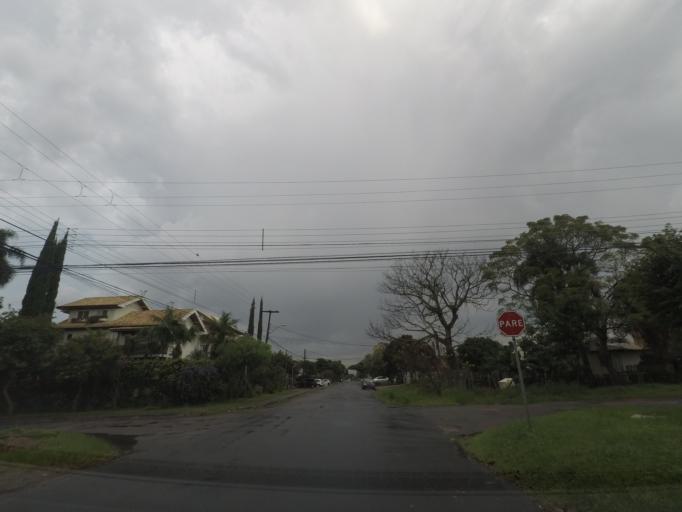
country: BR
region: Parana
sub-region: Curitiba
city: Curitiba
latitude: -25.4745
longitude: -49.2453
